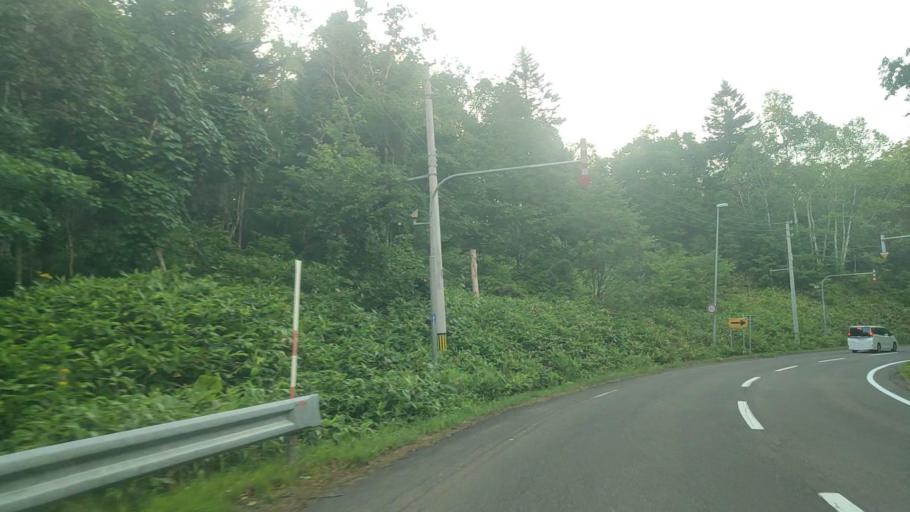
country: JP
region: Hokkaido
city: Bibai
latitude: 43.1743
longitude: 142.0686
